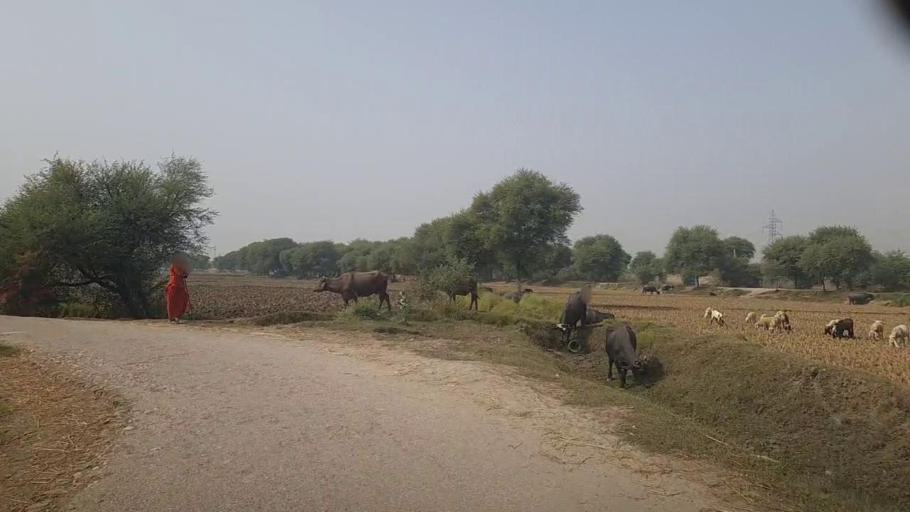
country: PK
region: Sindh
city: Kashmor
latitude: 28.3990
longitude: 69.4202
